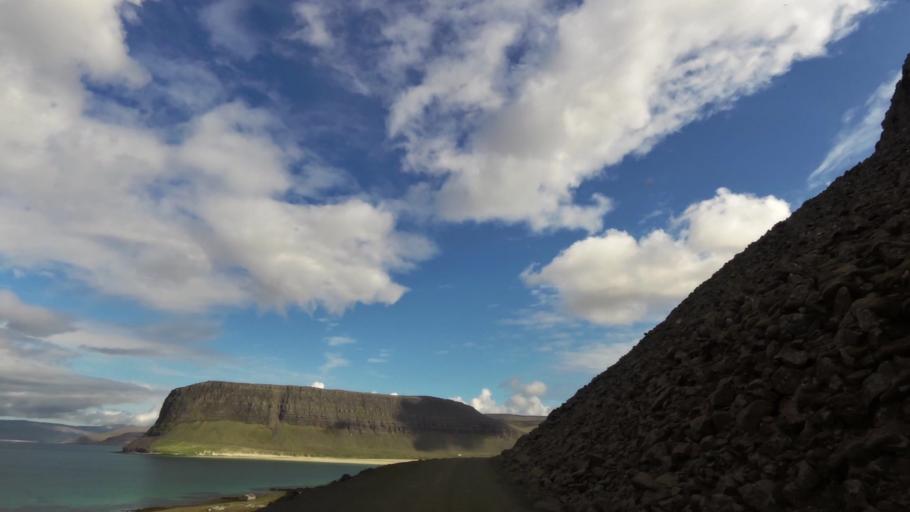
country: IS
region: West
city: Olafsvik
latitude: 65.5953
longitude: -24.1299
